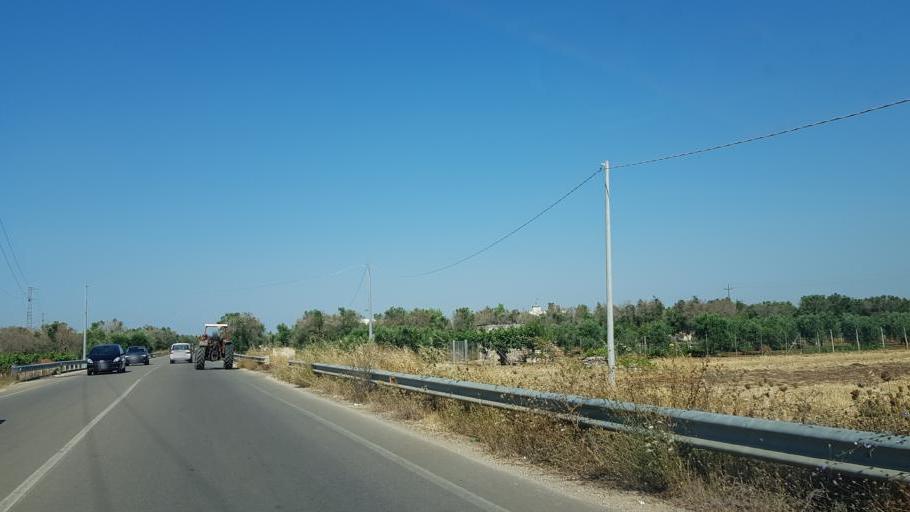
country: IT
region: Apulia
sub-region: Provincia di Lecce
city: Veglie
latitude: 40.3490
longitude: 17.9625
